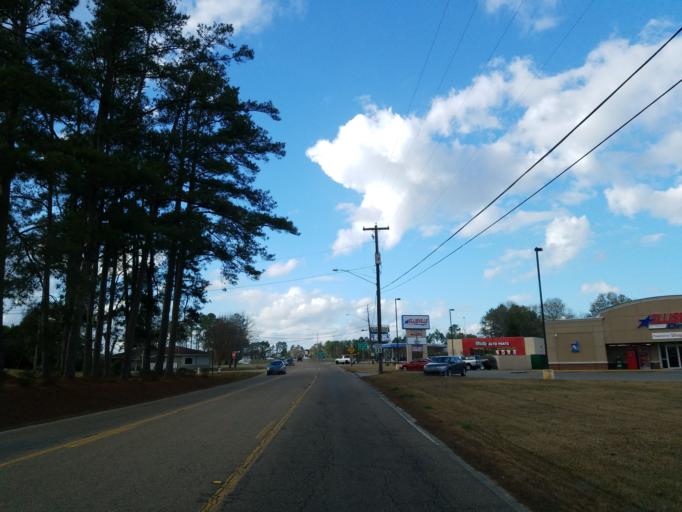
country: US
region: Mississippi
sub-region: Jones County
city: Ellisville
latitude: 31.6101
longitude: -89.2046
